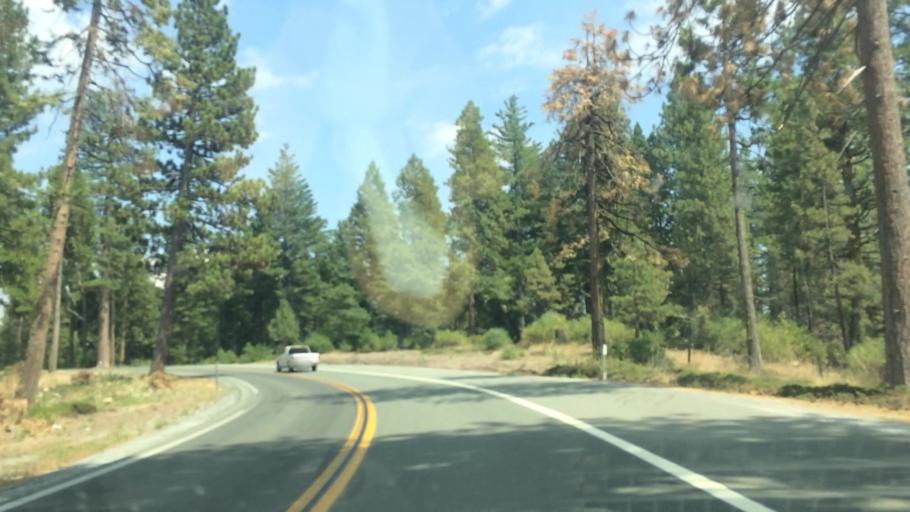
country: US
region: California
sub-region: Amador County
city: Pioneer
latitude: 38.5288
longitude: -120.4280
